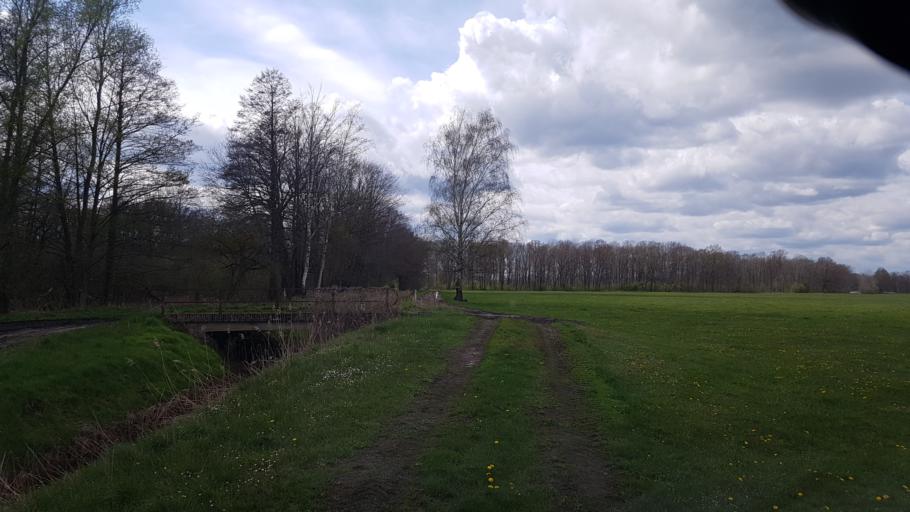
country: DE
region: Brandenburg
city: Bronkow
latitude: 51.6155
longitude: 13.9289
